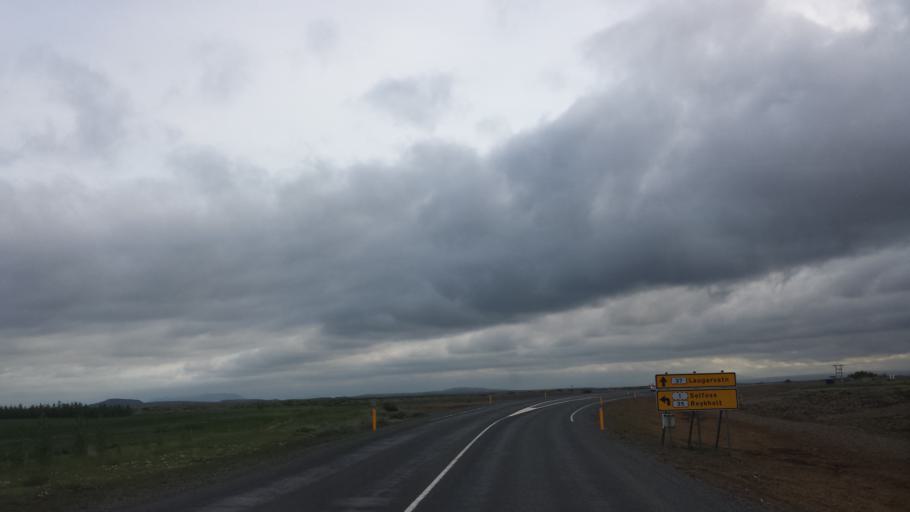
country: IS
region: South
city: Selfoss
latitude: 64.2745
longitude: -20.3539
